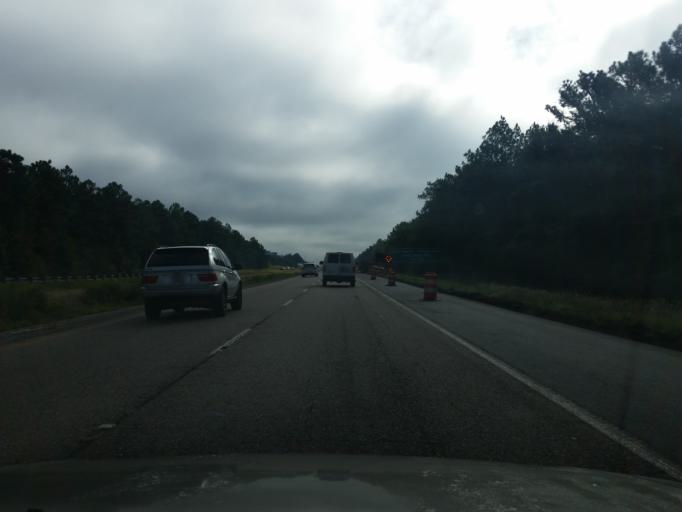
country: US
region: Alabama
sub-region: Baldwin County
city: Loxley
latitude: 30.6518
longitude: -87.7797
